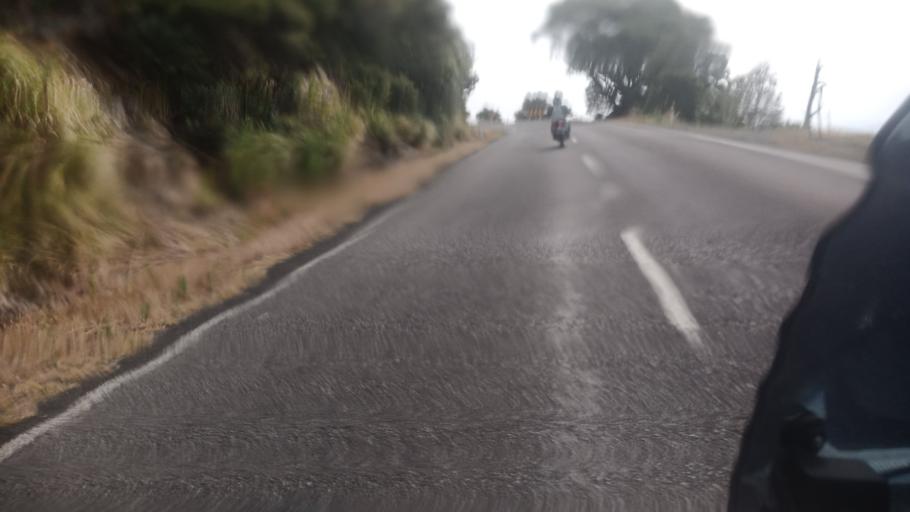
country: NZ
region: Bay of Plenty
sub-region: Opotiki District
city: Opotiki
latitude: -37.8688
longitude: 177.5908
